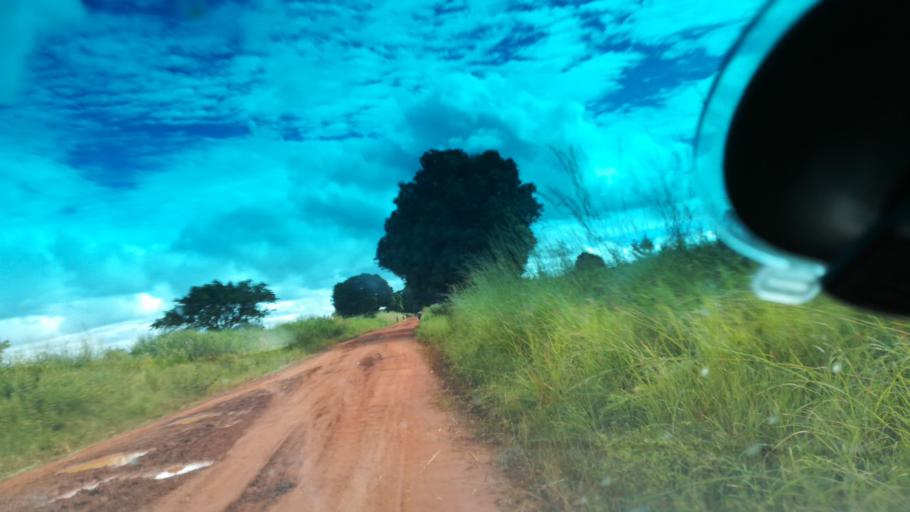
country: ZM
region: Luapula
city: Nchelenge
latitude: -9.1908
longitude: 28.2808
